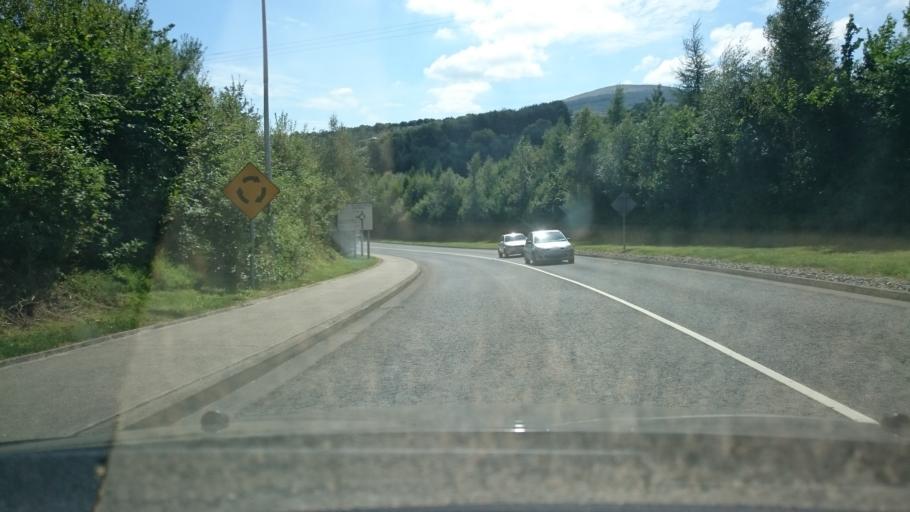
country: IE
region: Leinster
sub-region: Kilkenny
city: Graiguenamanagh
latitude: 52.5389
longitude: -6.9642
